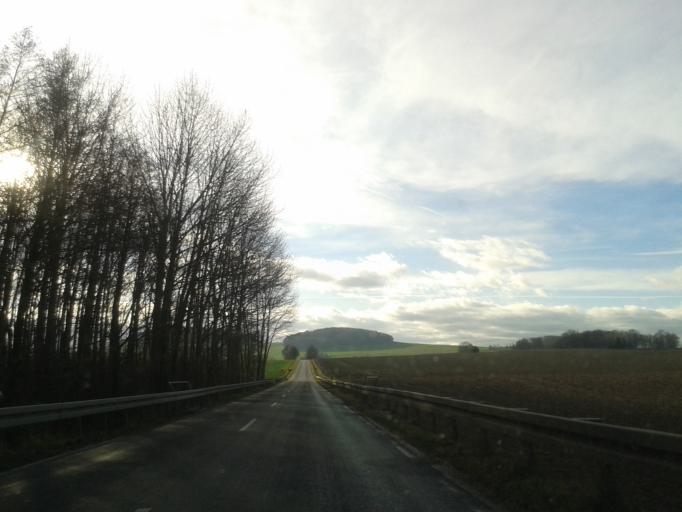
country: DE
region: Saxony
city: Eibau
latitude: 50.9840
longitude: 14.7018
